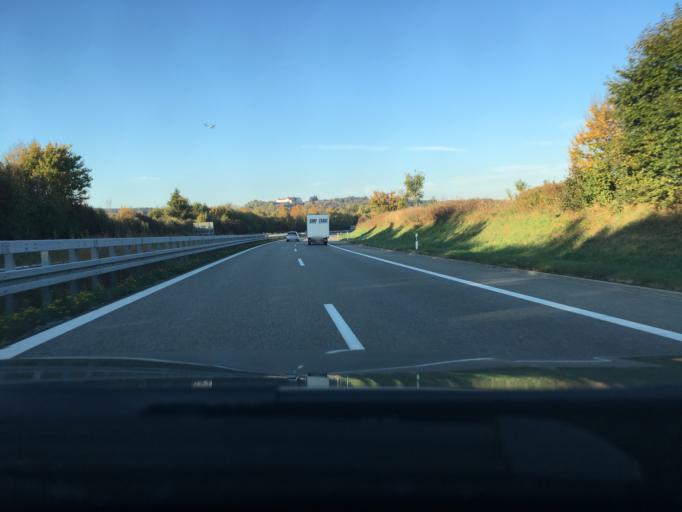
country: DE
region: Baden-Wuerttemberg
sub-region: Tuebingen Region
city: Leutkirch im Allgau
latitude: 47.8446
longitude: 9.9906
